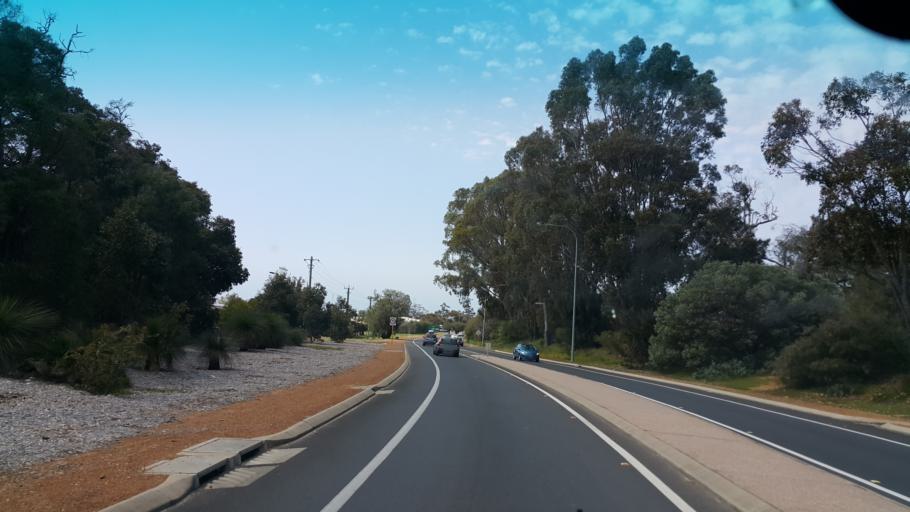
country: AU
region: Western Australia
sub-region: Busselton
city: Dunsborough
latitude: -33.6174
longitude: 115.1017
